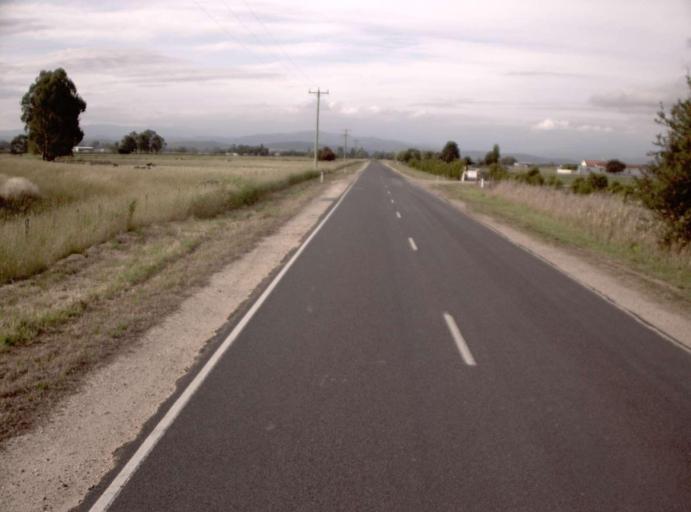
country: AU
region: Victoria
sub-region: Wellington
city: Sale
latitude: -37.9049
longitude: 146.9943
